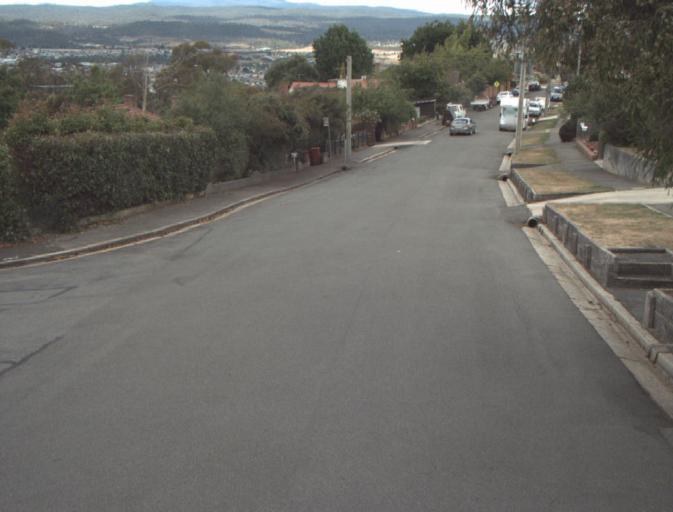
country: AU
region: Tasmania
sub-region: Launceston
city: West Launceston
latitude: -41.4396
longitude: 147.1144
